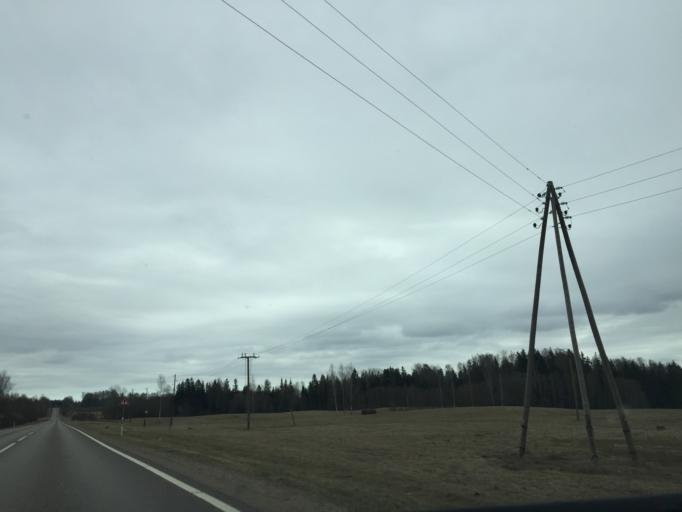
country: LV
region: Kraslavas Rajons
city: Kraslava
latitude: 55.9117
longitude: 27.0658
